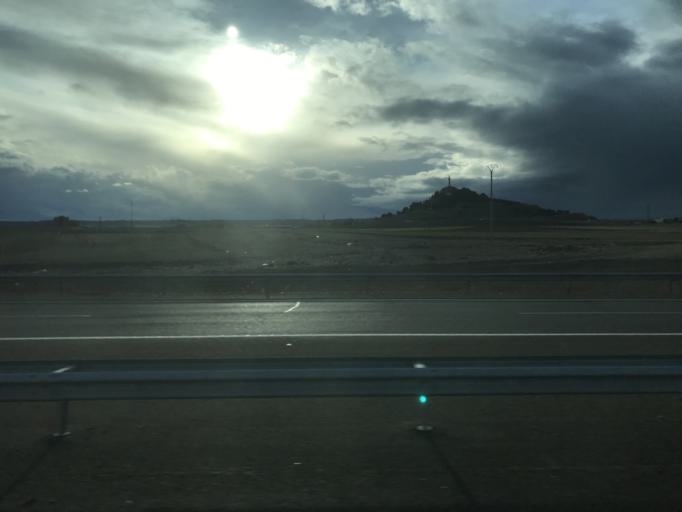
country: ES
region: Castille and Leon
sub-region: Provincia de Palencia
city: Villalobon
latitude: 42.0286
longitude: -4.5160
